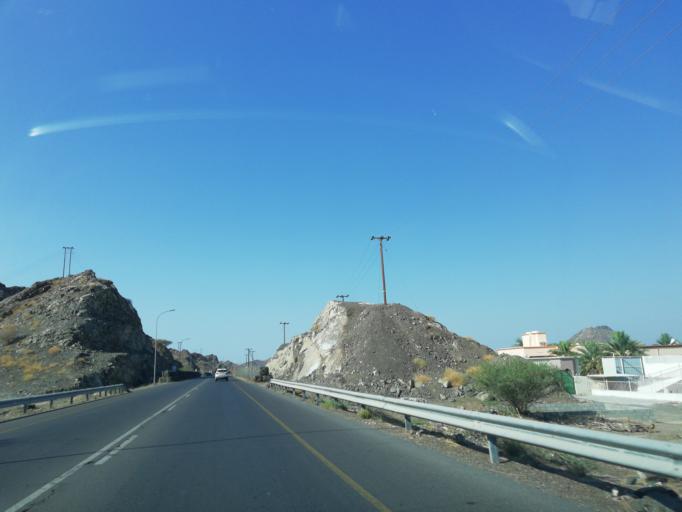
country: OM
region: Ash Sharqiyah
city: Ibra'
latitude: 22.8326
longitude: 58.1714
